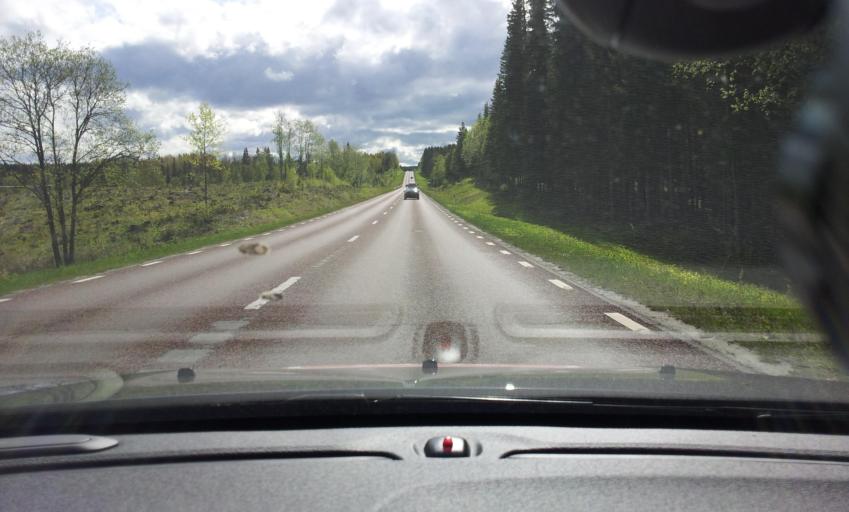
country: SE
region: Jaemtland
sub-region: OEstersunds Kommun
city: Brunflo
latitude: 63.0263
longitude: 14.7591
